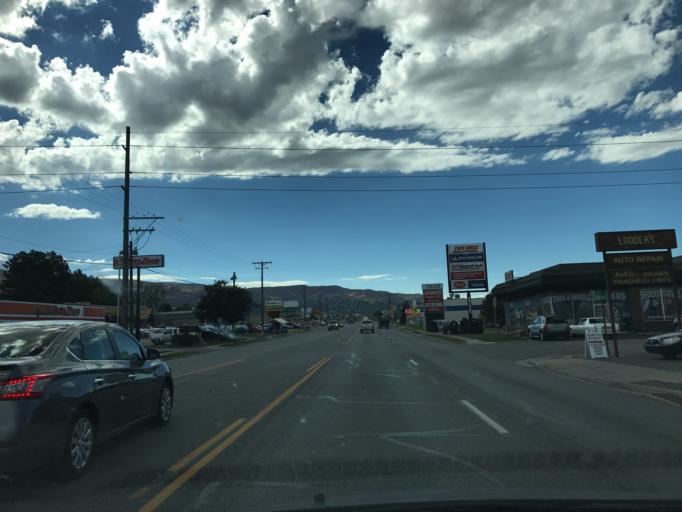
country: US
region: Utah
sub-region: Davis County
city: Woods Cross
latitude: 40.8832
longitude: -111.8923
